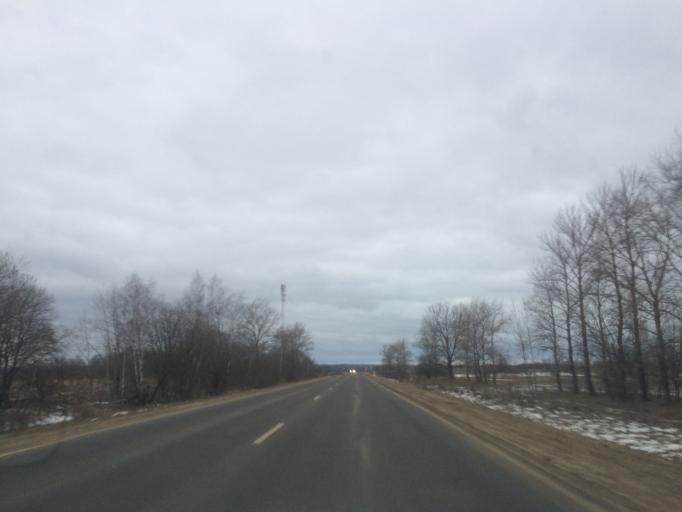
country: RU
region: Tula
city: Odoyev
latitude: 53.9949
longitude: 36.7453
